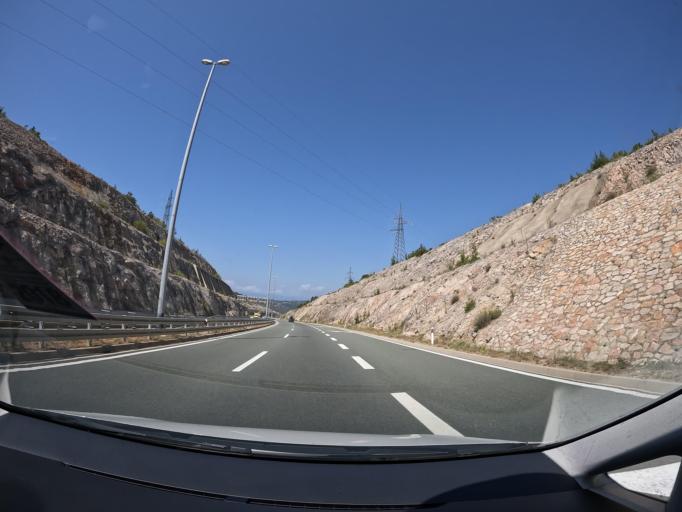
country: HR
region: Primorsko-Goranska
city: Hreljin
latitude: 45.2897
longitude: 14.6768
